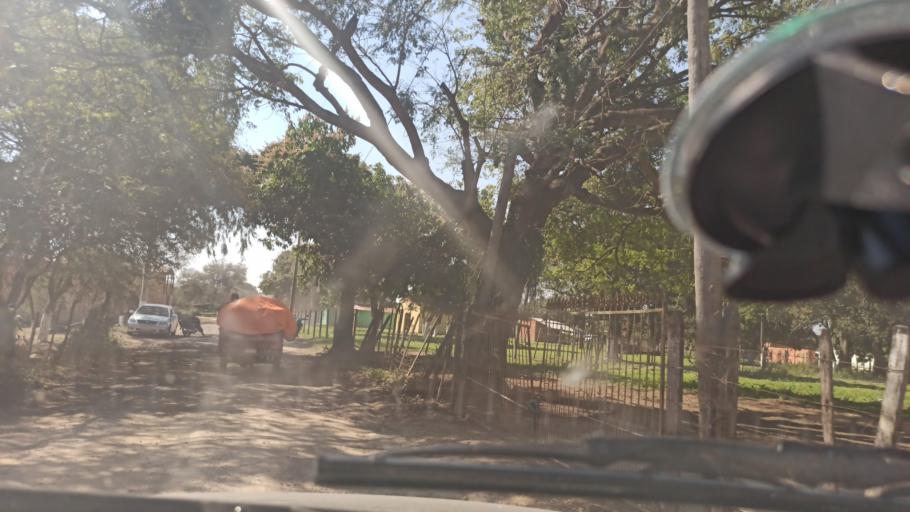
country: AR
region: Formosa
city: Clorinda
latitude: -25.2984
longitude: -57.7058
